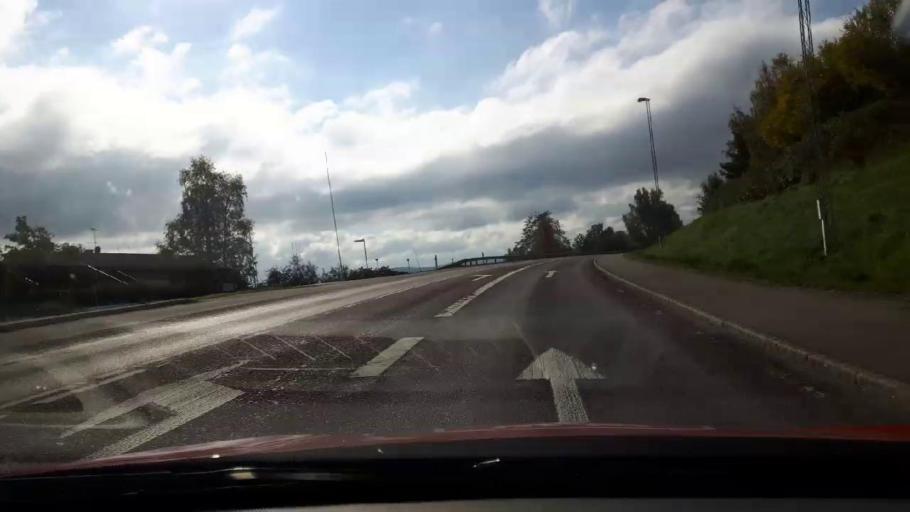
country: SE
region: Gaevleborg
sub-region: Ljusdals Kommun
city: Jaervsoe
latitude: 61.7023
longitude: 16.1652
